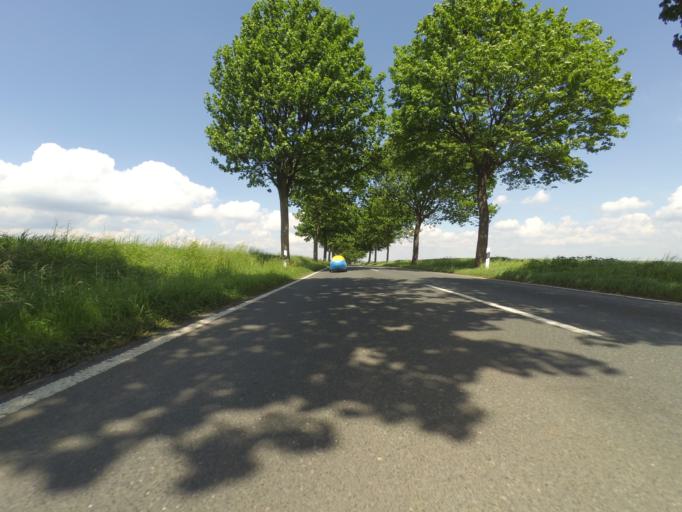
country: DE
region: Lower Saxony
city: Hohenhameln
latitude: 52.2075
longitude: 10.0370
